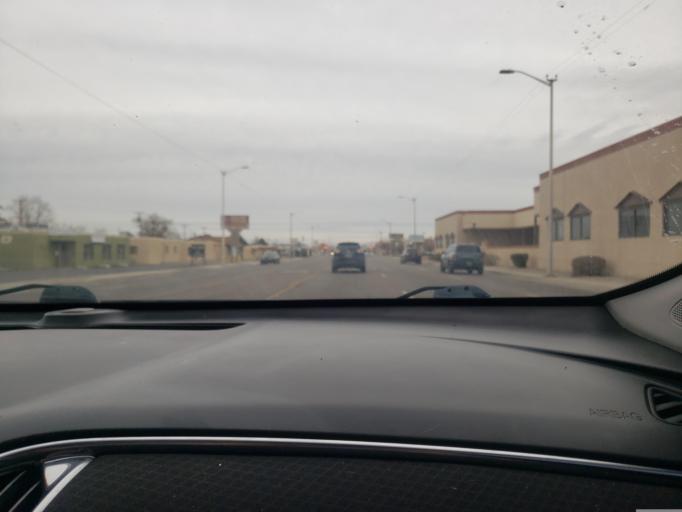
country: US
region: New Mexico
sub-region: Bernalillo County
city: Lee Acres
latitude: 35.1134
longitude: -106.5863
